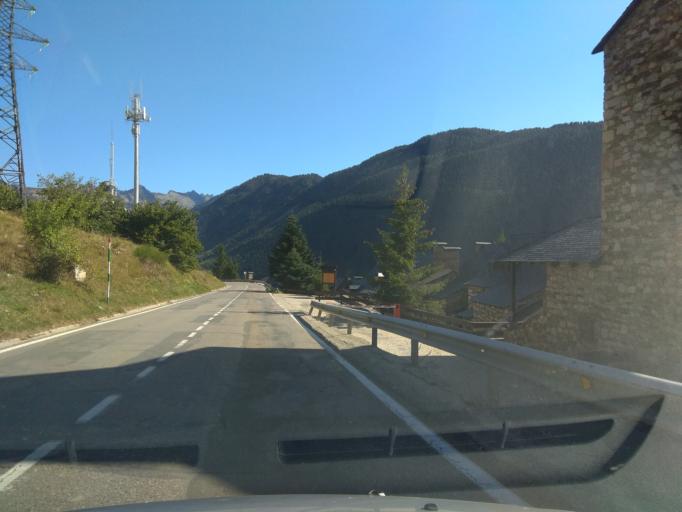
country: ES
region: Catalonia
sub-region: Provincia de Lleida
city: Vielha
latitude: 42.7014
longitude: 0.9331
